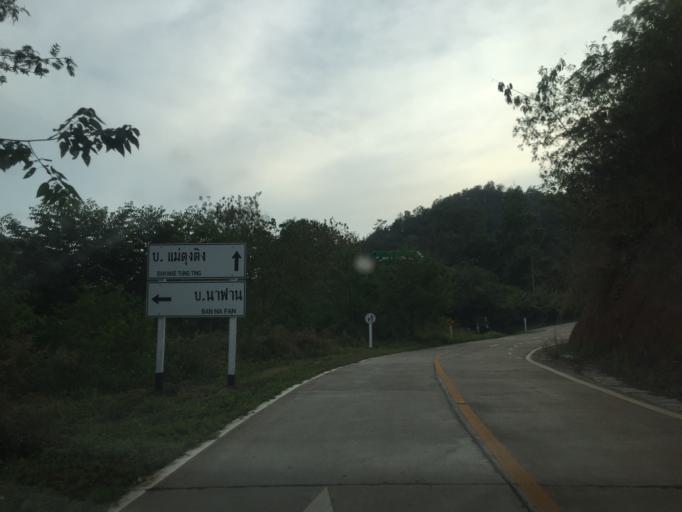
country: TH
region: Chiang Mai
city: Samoeng
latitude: 18.9667
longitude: 98.7171
